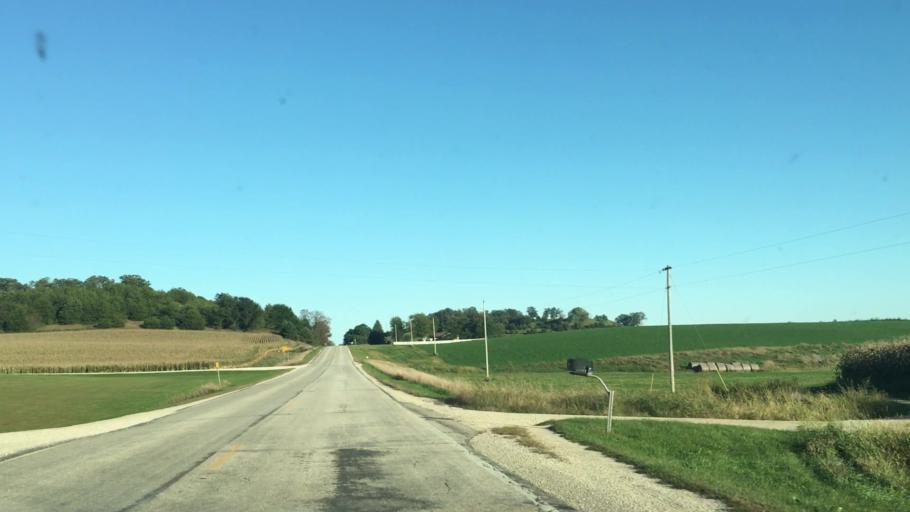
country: US
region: Minnesota
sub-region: Fillmore County
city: Chatfield
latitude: 43.8427
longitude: -92.0908
